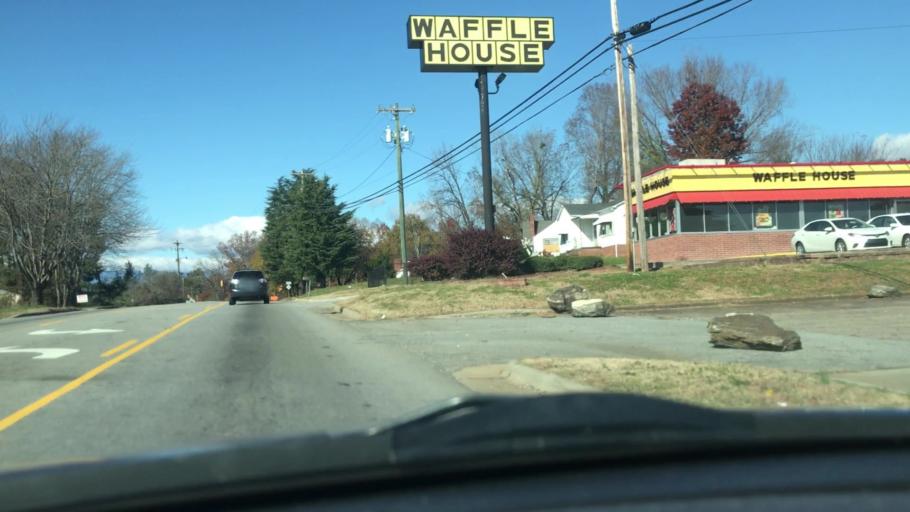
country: US
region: North Carolina
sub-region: McDowell County
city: Marion
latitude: 35.6593
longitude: -81.9640
